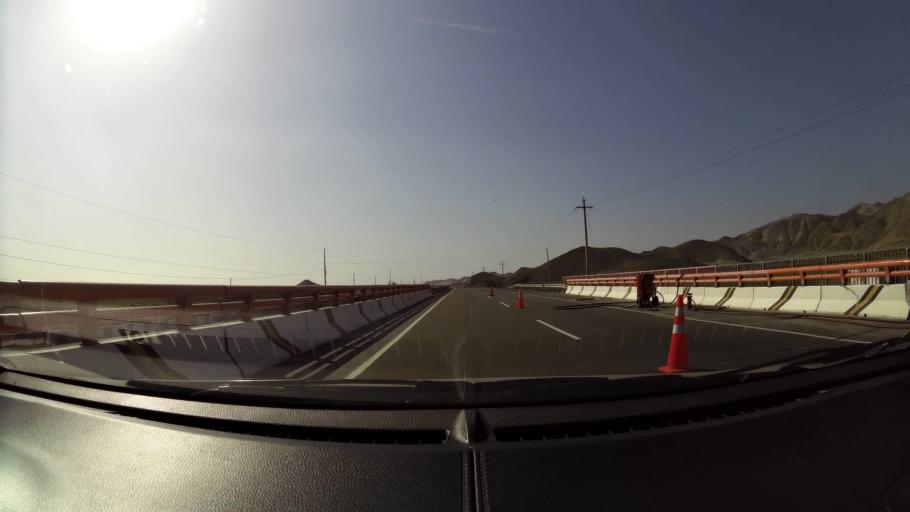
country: PE
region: Ancash
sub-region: Provincia de Huarmey
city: La Caleta Culebras
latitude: -9.9368
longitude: -78.2183
